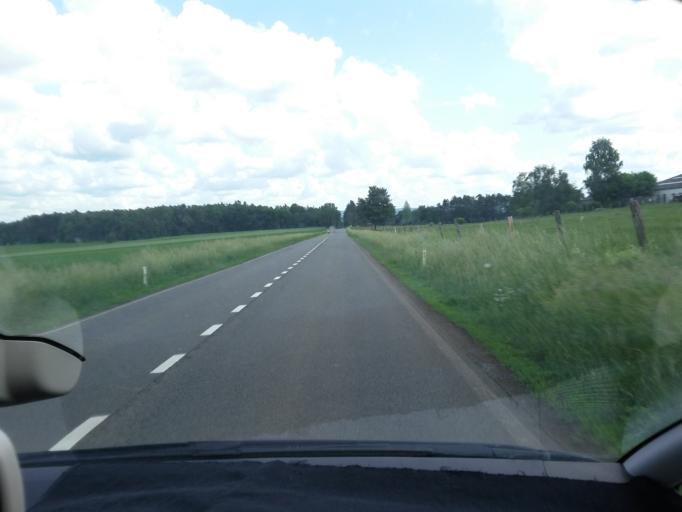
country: BE
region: Wallonia
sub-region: Province de Namur
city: Rochefort
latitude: 50.1367
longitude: 5.2270
